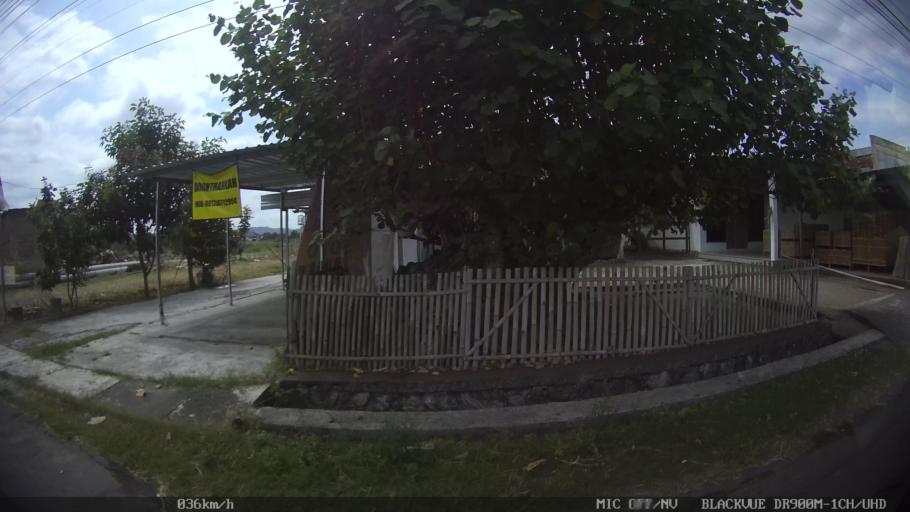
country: ID
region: Daerah Istimewa Yogyakarta
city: Depok
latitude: -7.7876
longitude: 110.4636
